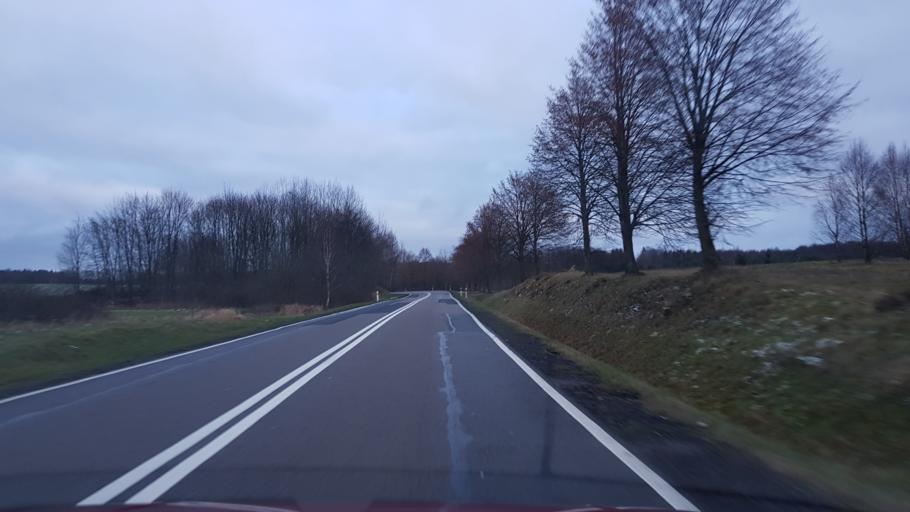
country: PL
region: Pomeranian Voivodeship
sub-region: Powiat bytowski
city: Tuchomie
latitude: 54.0641
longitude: 17.2533
